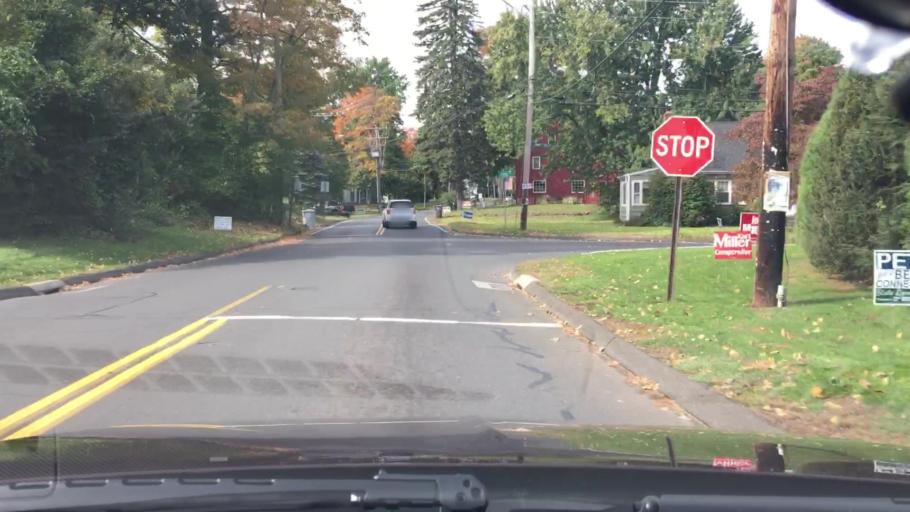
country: US
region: Connecticut
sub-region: Hartford County
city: Plainville
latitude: 41.6782
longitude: -72.8889
